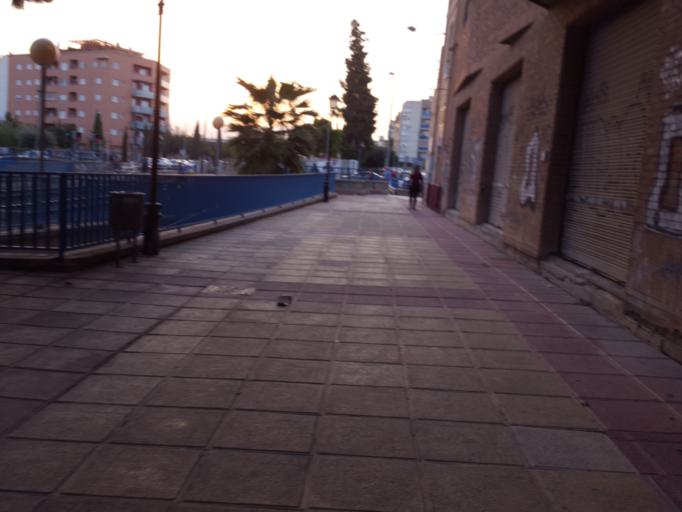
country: ES
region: Murcia
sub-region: Murcia
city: Murcia
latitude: 37.9750
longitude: -1.1334
